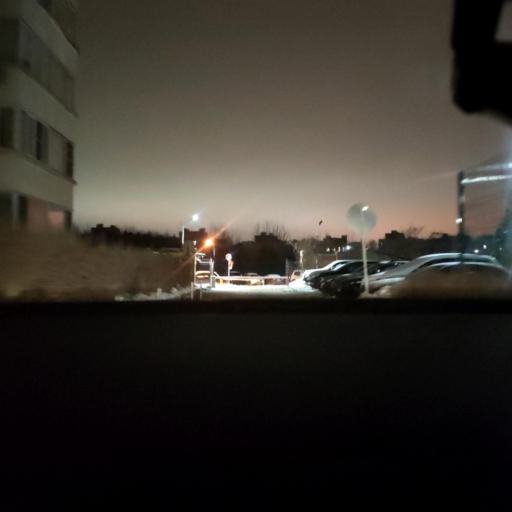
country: RU
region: Moskovskaya
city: Zarech'ye
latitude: 55.6760
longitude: 37.3867
